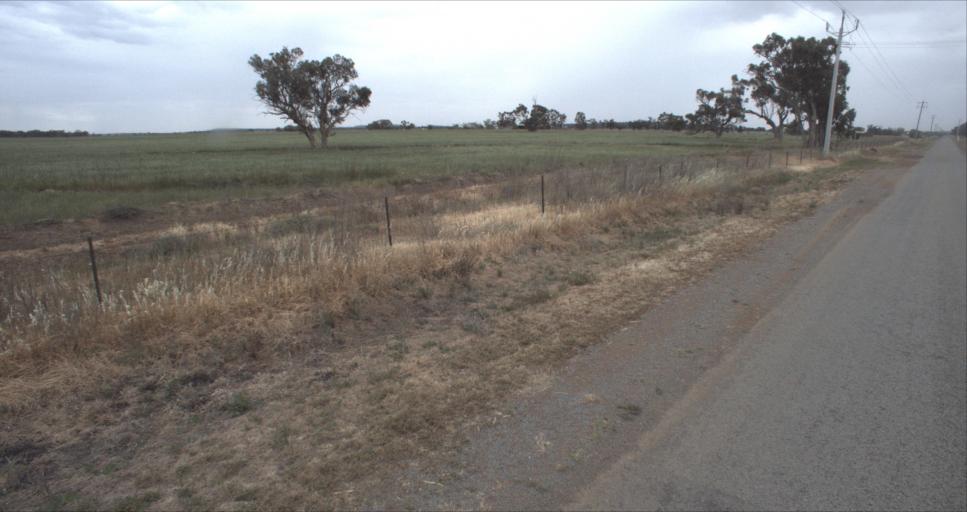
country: AU
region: New South Wales
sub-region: Leeton
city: Leeton
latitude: -34.4178
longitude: 146.3391
